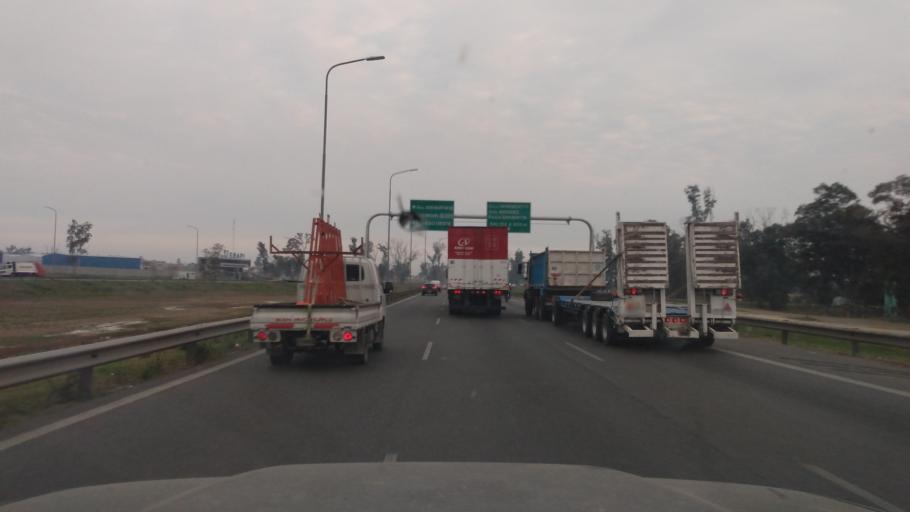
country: AR
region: Buenos Aires
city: Hurlingham
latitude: -34.5263
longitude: -58.5937
